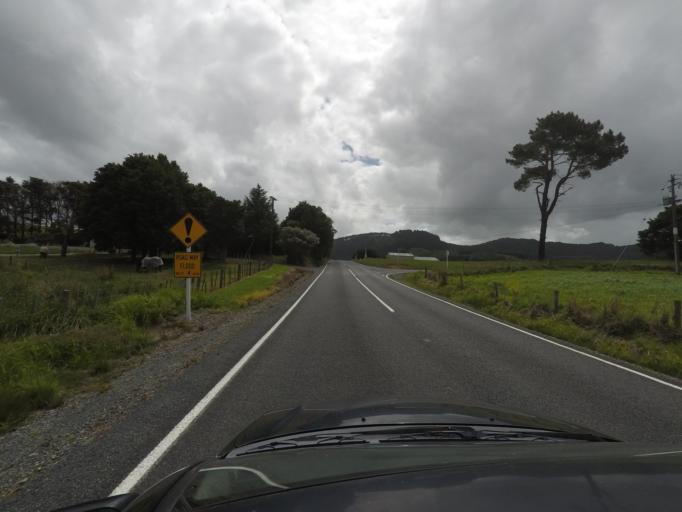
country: NZ
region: Auckland
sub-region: Auckland
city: Parakai
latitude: -36.4998
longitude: 174.4977
